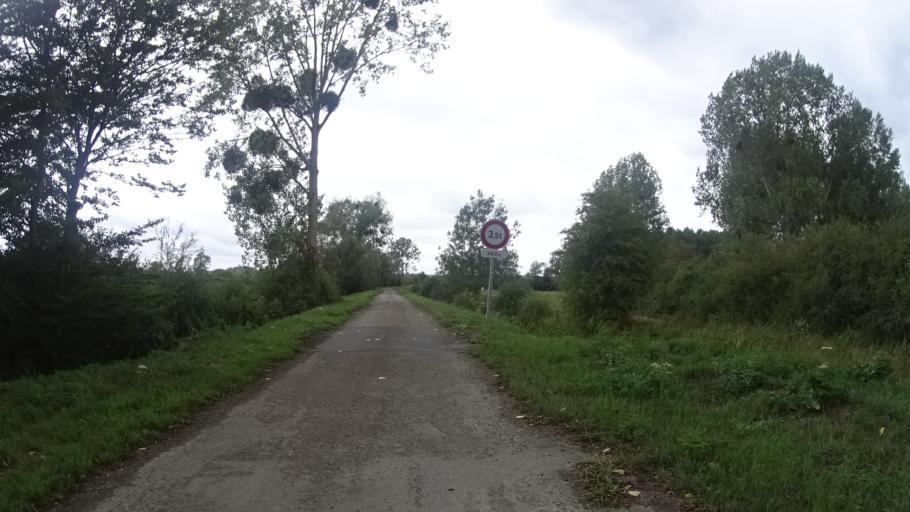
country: FR
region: Nord-Pas-de-Calais
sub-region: Departement du Nord
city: Maroilles
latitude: 50.1484
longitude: 3.7546
